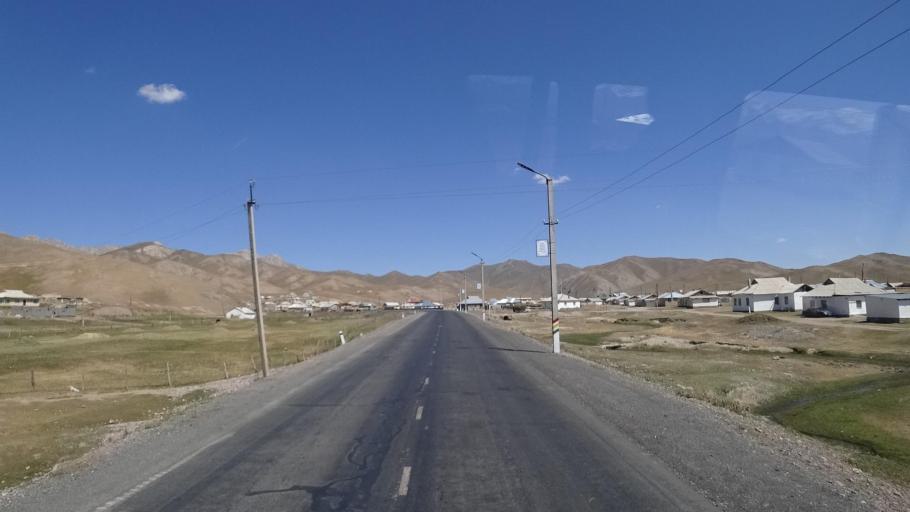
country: KG
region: Osh
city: Gul'cha
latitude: 39.7217
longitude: 73.2468
